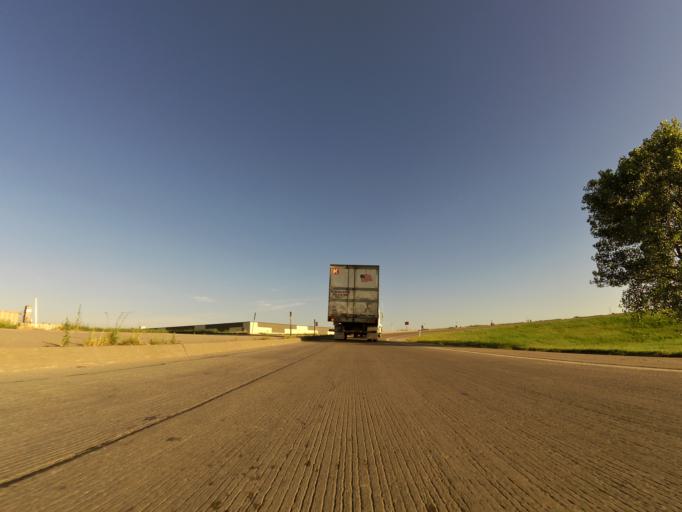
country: US
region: Kansas
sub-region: Sedgwick County
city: Wichita
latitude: 37.7384
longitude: -97.3200
